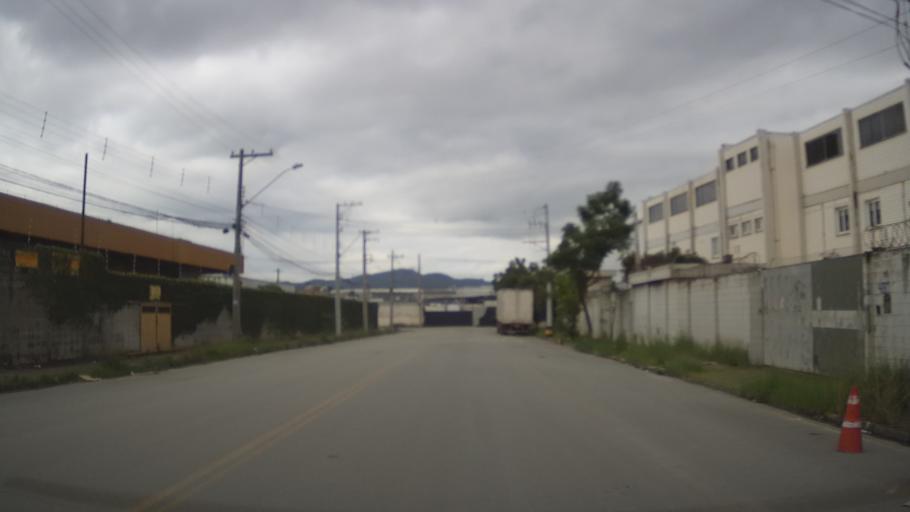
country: BR
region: Sao Paulo
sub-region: Guarulhos
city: Guarulhos
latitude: -23.4343
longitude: -46.5000
